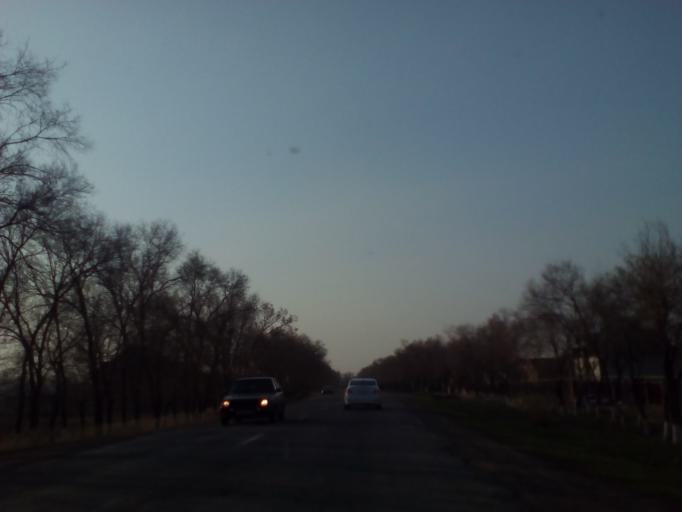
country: KZ
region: Almaty Oblysy
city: Burunday
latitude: 43.1778
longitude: 76.5209
